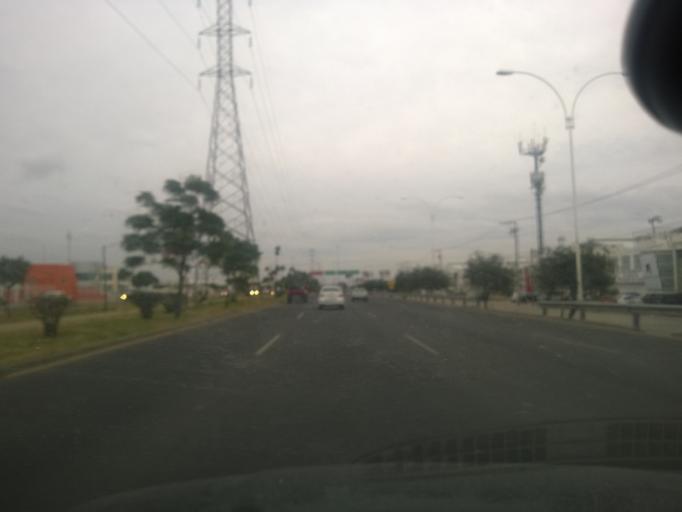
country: MX
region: Guanajuato
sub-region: Leon
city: Medina
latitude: 21.1183
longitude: -101.6268
